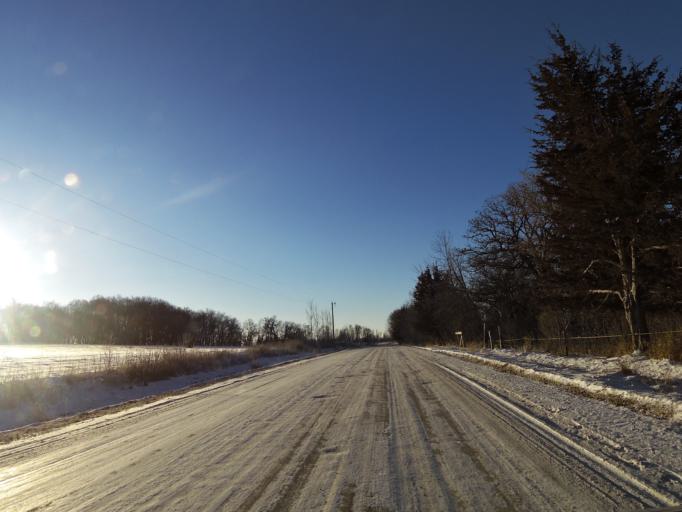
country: US
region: Minnesota
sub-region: Scott County
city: Jordan
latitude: 44.6477
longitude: -93.5162
